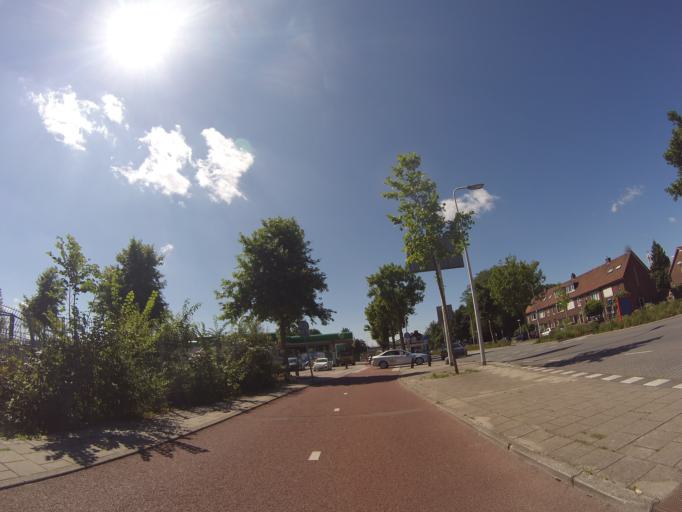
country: NL
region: Utrecht
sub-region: Gemeente Utrecht
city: Utrecht
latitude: 52.0989
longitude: 5.0866
